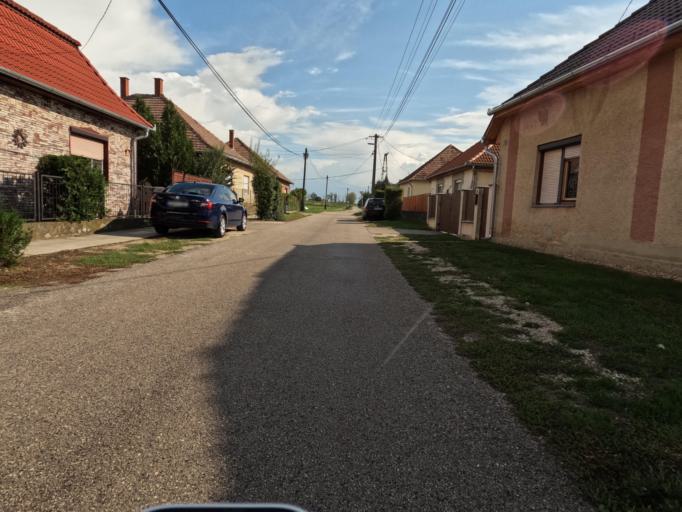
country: HU
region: Tolna
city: Tengelic
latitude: 46.5233
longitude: 18.7098
